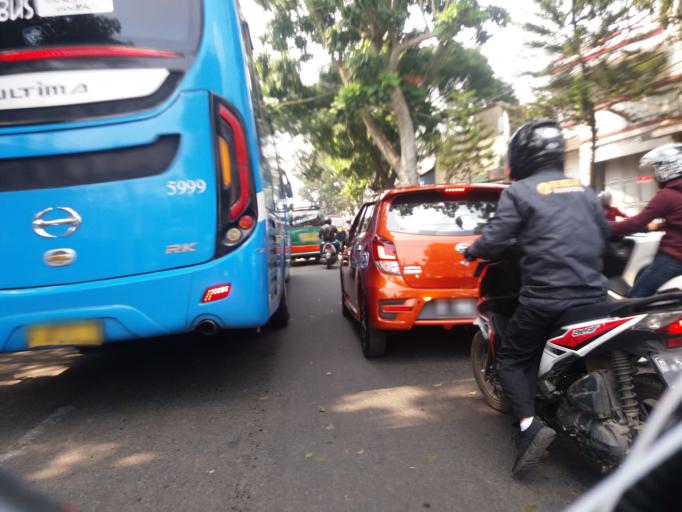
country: ID
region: West Java
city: Bandung
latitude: -6.9157
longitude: 107.5852
